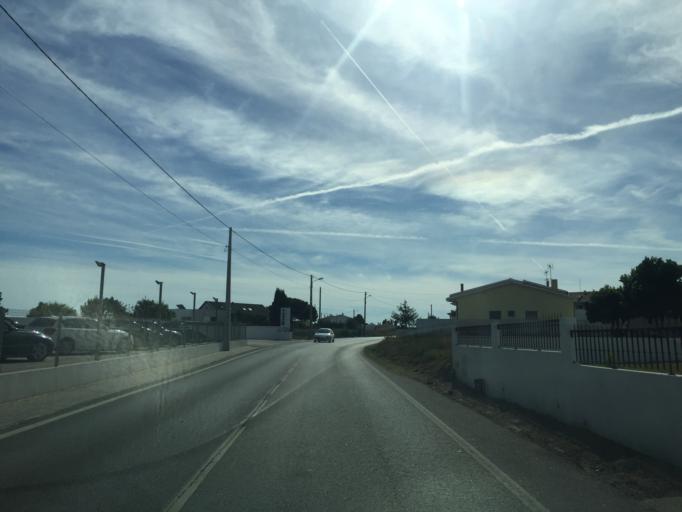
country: PT
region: Coimbra
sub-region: Figueira da Foz
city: Lavos
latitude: 40.0729
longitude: -8.8189
